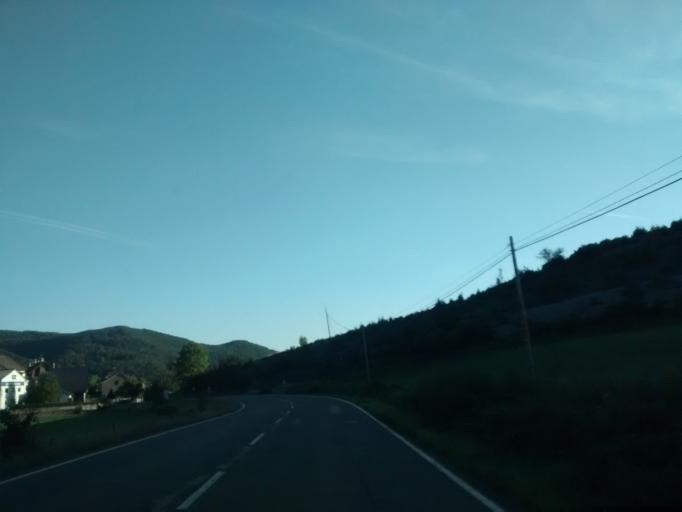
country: ES
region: Aragon
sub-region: Provincia de Huesca
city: Anso
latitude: 42.7437
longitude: -0.7485
